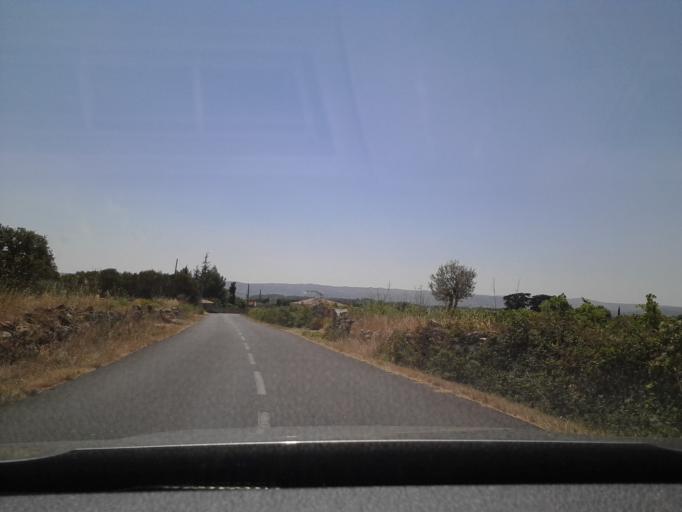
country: FR
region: Languedoc-Roussillon
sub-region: Departement de l'Herault
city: Montpeyroux
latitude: 43.7035
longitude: 3.4931
